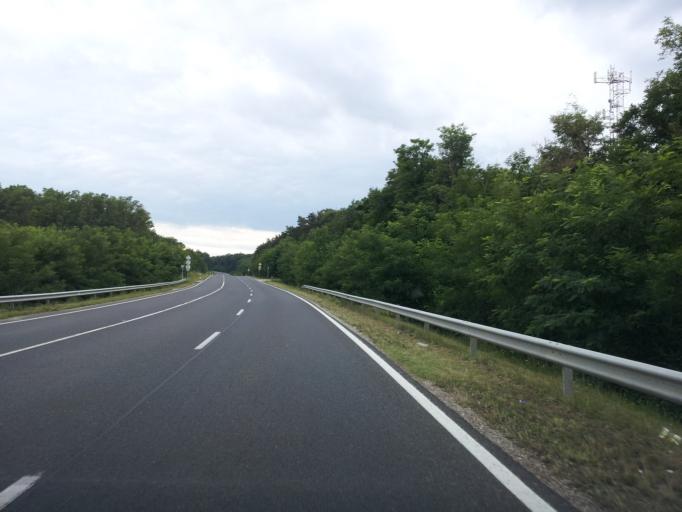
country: HU
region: Vas
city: Sarvar
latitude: 47.1080
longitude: 16.9720
